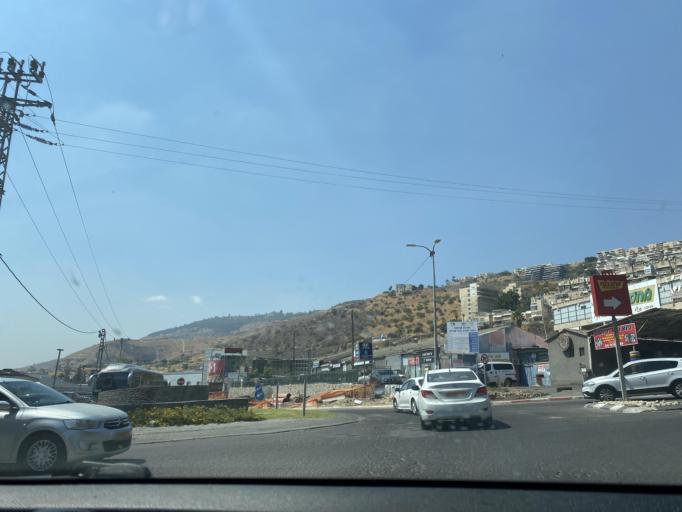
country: IL
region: Northern District
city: Tiberias
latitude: 32.7904
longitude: 35.5329
